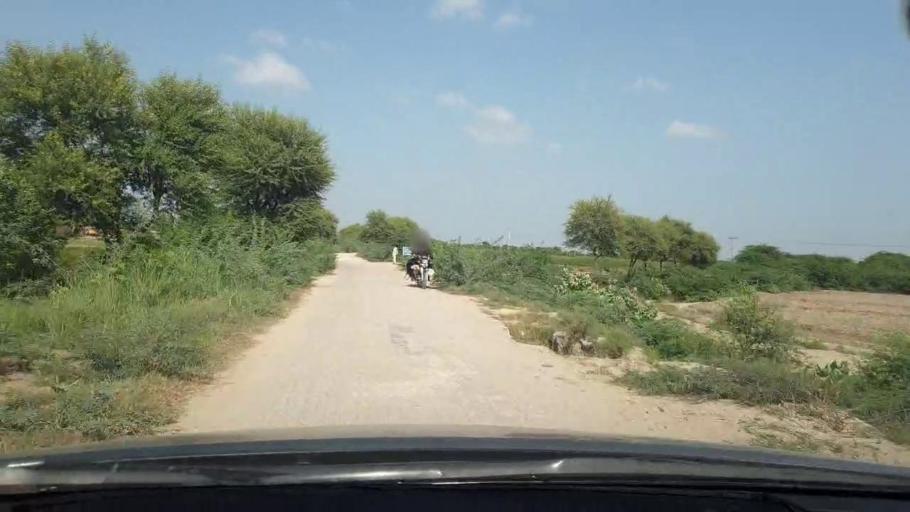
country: PK
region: Sindh
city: Naukot
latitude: 24.8840
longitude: 69.2717
